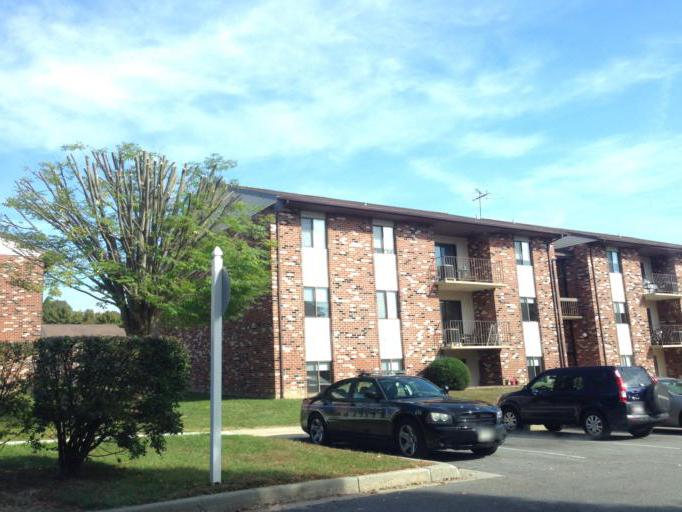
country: US
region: Maryland
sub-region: Howard County
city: Ellicott City
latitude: 39.2798
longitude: -76.8353
